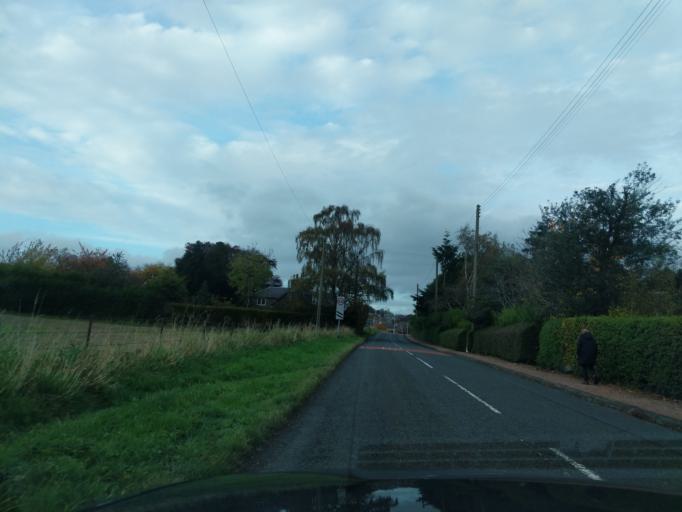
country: GB
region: Scotland
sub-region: Fife
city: Tayport
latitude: 56.4399
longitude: -2.8844
